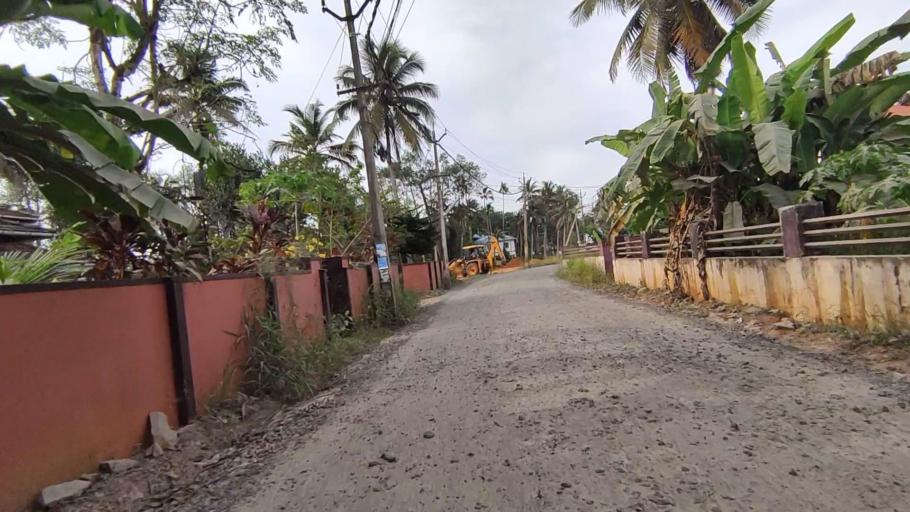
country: IN
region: Kerala
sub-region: Kottayam
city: Kottayam
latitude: 9.5869
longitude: 76.4921
